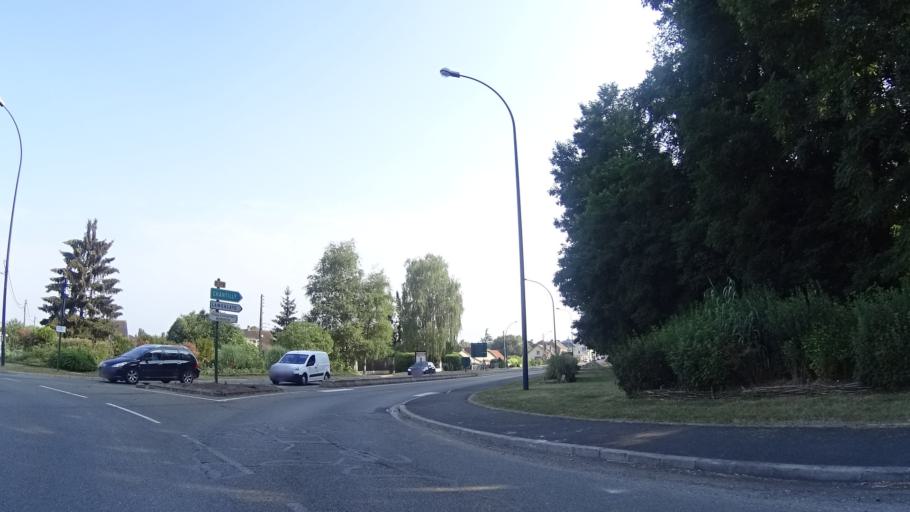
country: FR
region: Ile-de-France
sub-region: Departement du Val-d'Oise
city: Chaumontel
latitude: 49.1234
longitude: 2.4274
